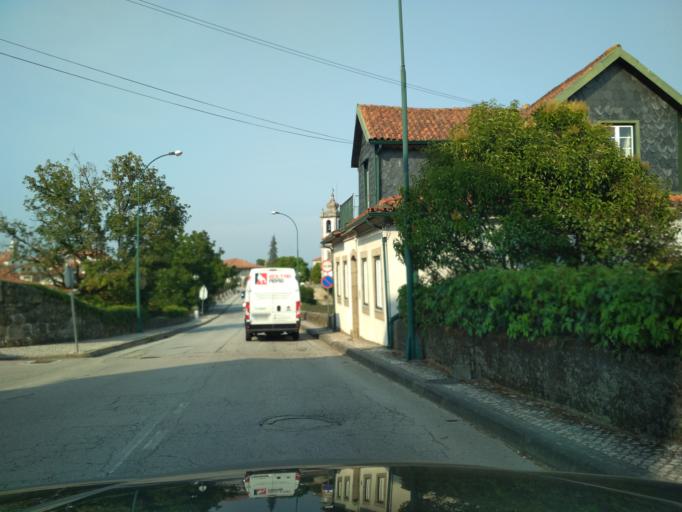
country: PT
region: Viseu
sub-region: Santa Comba Dao
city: Santa Comba Dao
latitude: 40.3946
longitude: -8.1324
